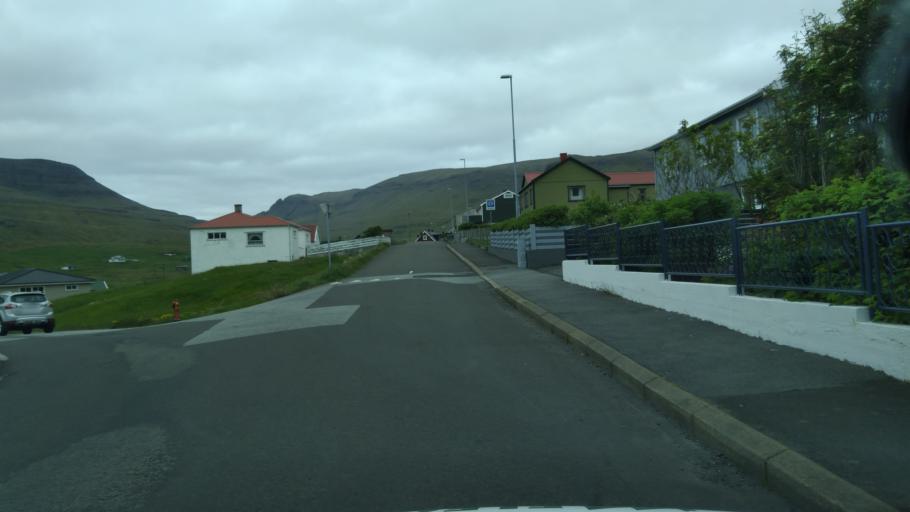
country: FO
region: Suduroy
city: Tvoroyri
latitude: 61.5632
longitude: -6.8385
